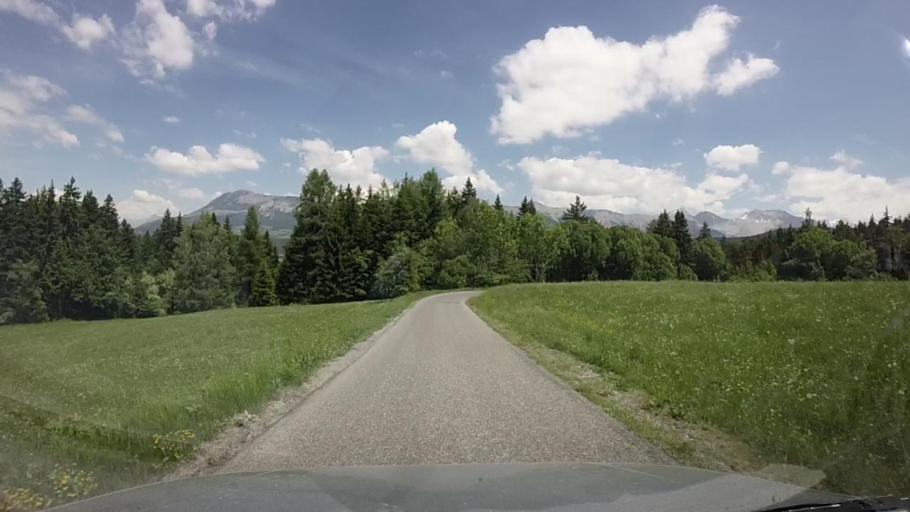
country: FR
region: Provence-Alpes-Cote d'Azur
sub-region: Departement des Alpes-de-Haute-Provence
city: Seyne-les-Alpes
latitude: 44.3322
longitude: 6.3323
